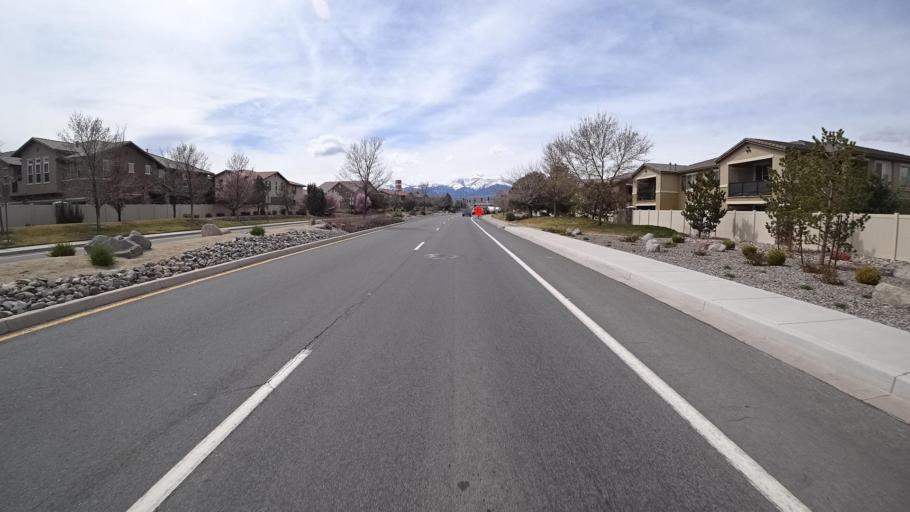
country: US
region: Nevada
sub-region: Washoe County
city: Sparks
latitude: 39.4235
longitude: -119.7310
